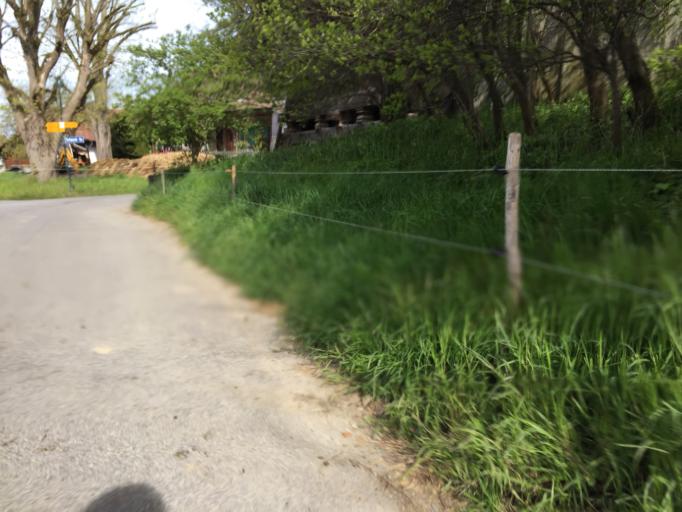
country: CH
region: Bern
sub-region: Bern-Mittelland District
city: Koniz
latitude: 46.9157
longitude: 7.3808
